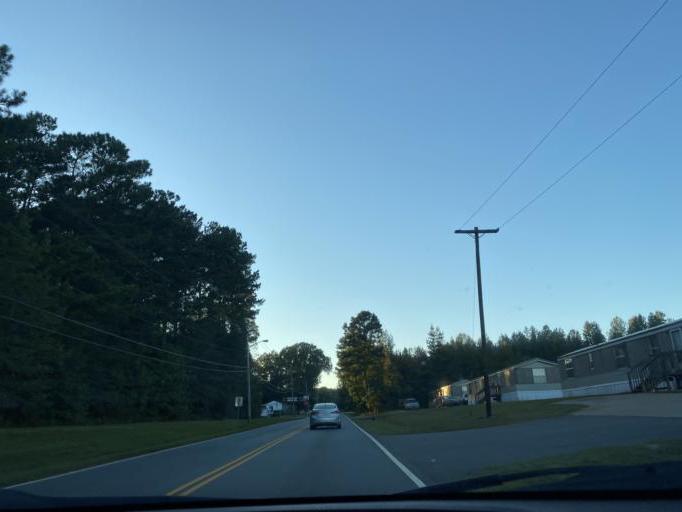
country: US
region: South Carolina
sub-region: Cherokee County
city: Gaffney
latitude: 35.0898
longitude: -81.6495
